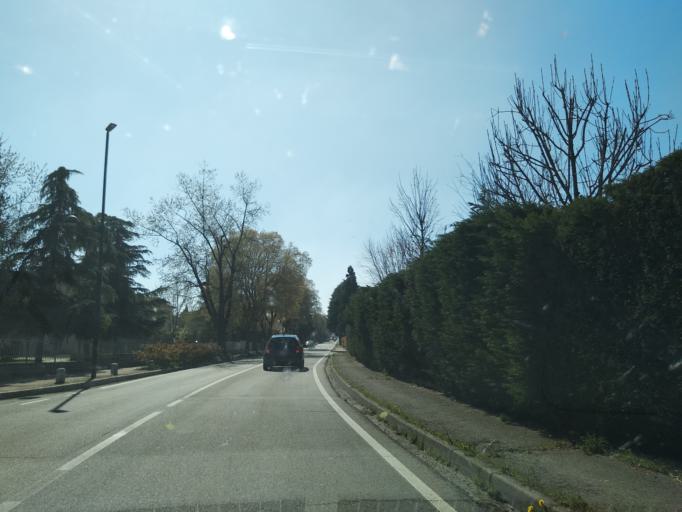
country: IT
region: Emilia-Romagna
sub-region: Provincia di Reggio Emilia
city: Albinea
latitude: 44.6251
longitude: 10.6060
